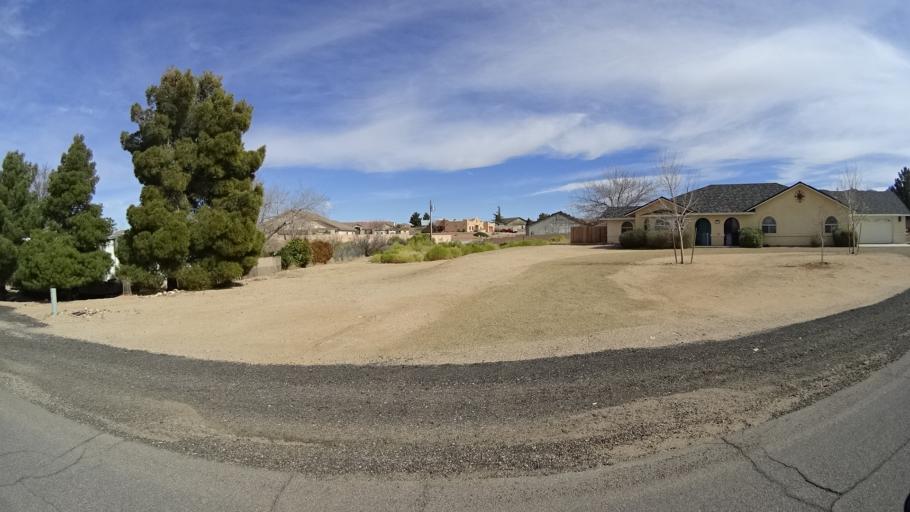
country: US
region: Arizona
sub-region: Mohave County
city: Kingman
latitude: 35.1905
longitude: -113.9828
